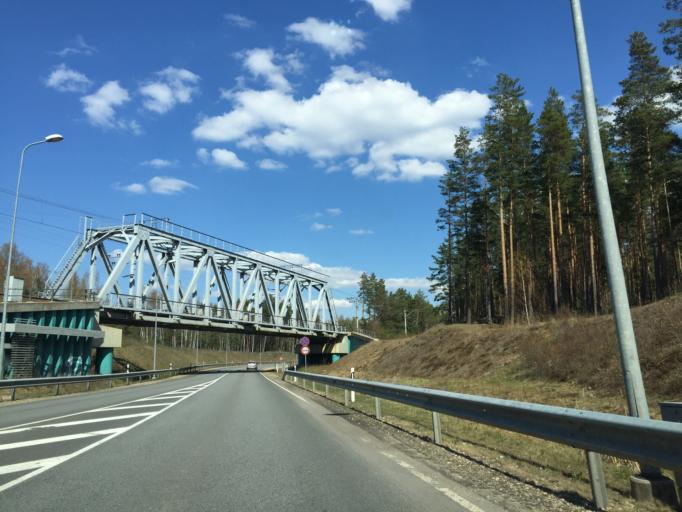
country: LV
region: Saulkrastu
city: Saulkrasti
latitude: 57.1959
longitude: 24.3639
